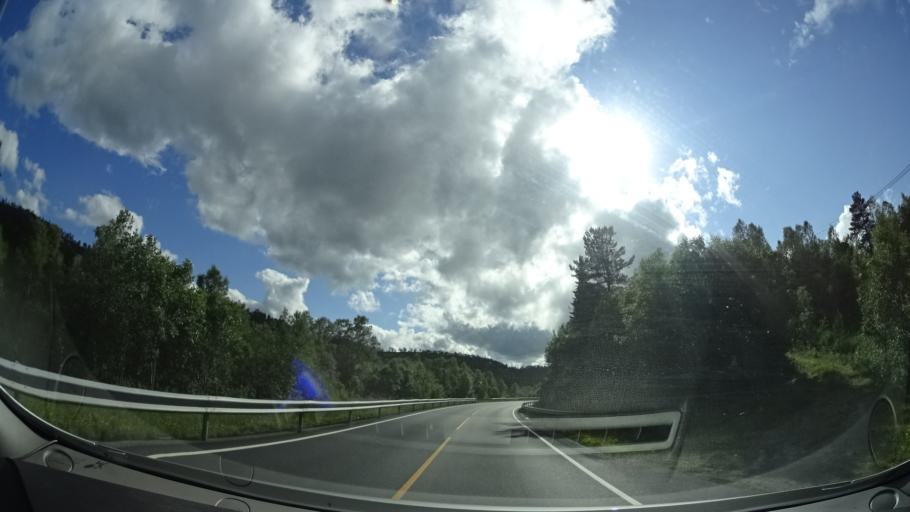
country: NO
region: More og Romsdal
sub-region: Rindal
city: Rindal
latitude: 63.2279
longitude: 9.3146
